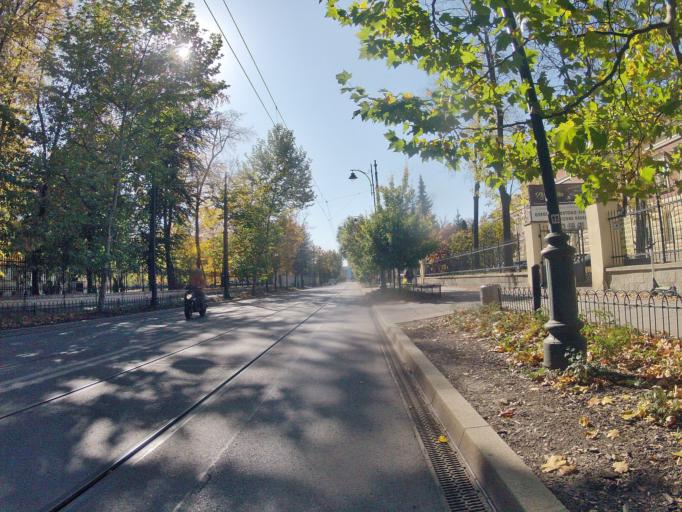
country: PL
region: Lesser Poland Voivodeship
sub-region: Krakow
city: Krakow
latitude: 50.0713
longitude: 19.9548
